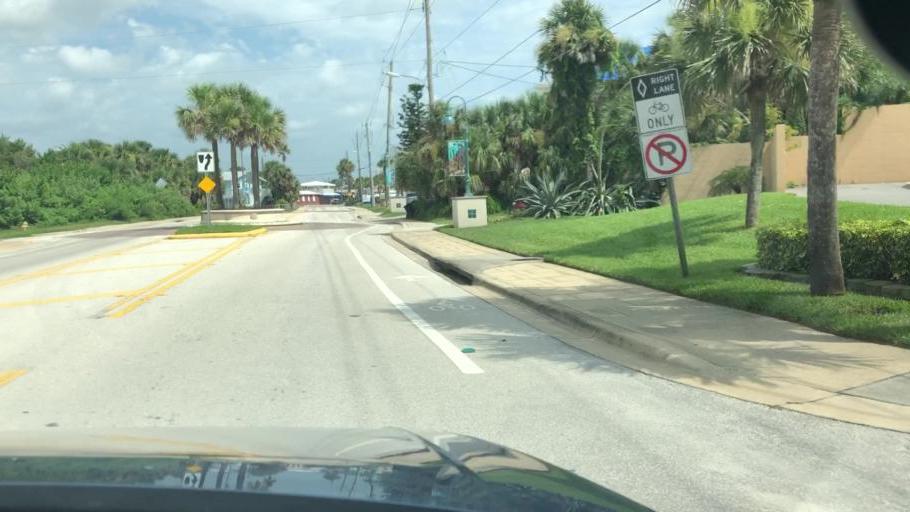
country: US
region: Florida
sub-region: Volusia County
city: New Smyrna Beach
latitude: 29.0365
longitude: -80.8956
